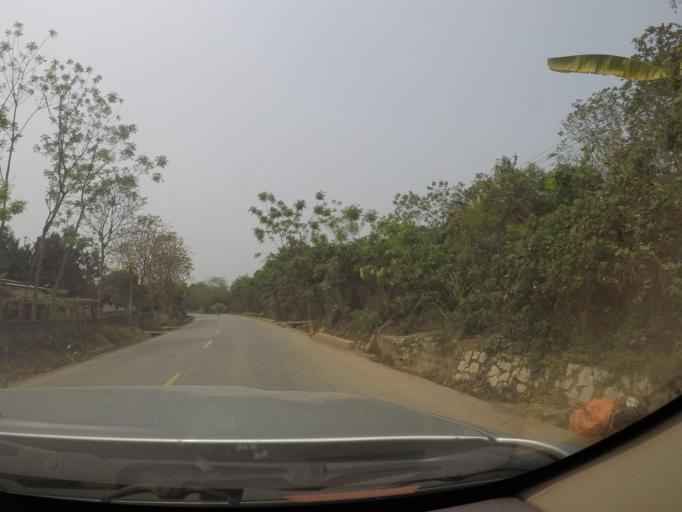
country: VN
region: Thanh Hoa
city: Thi Tran Cam Thuy
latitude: 20.1558
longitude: 105.4555
